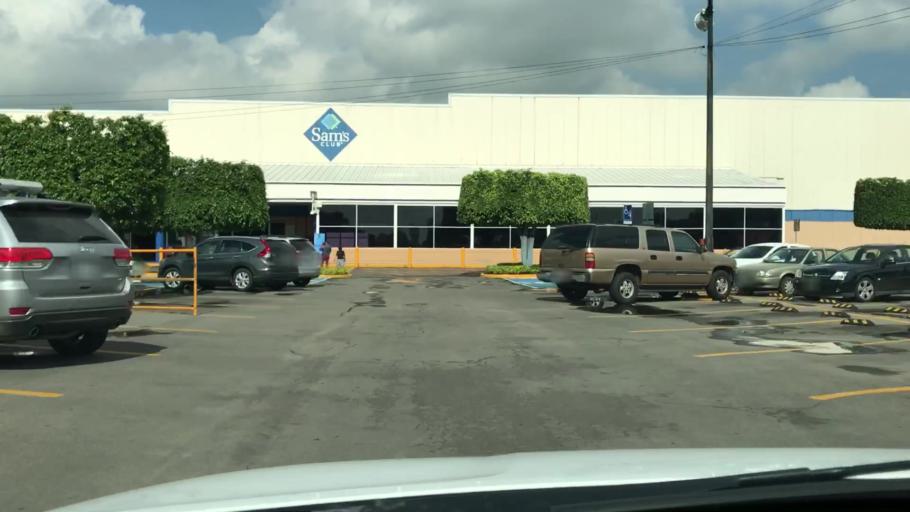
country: MX
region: Jalisco
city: Guadalajara
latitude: 20.6801
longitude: -103.4317
